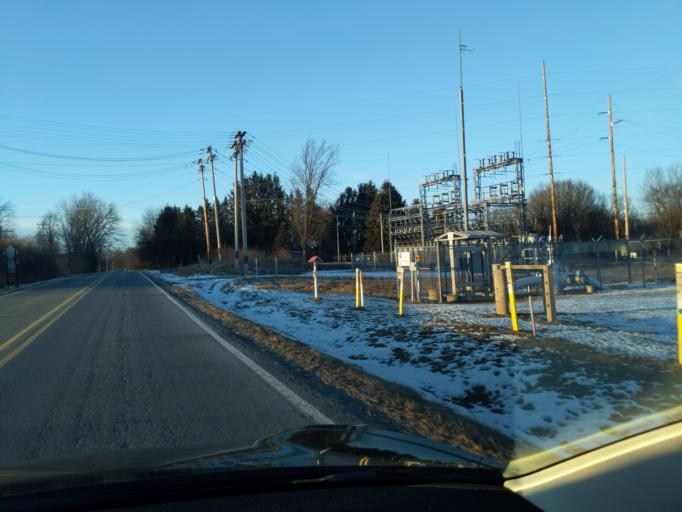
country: US
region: Michigan
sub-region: Ingham County
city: Stockbridge
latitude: 42.5040
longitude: -84.2550
